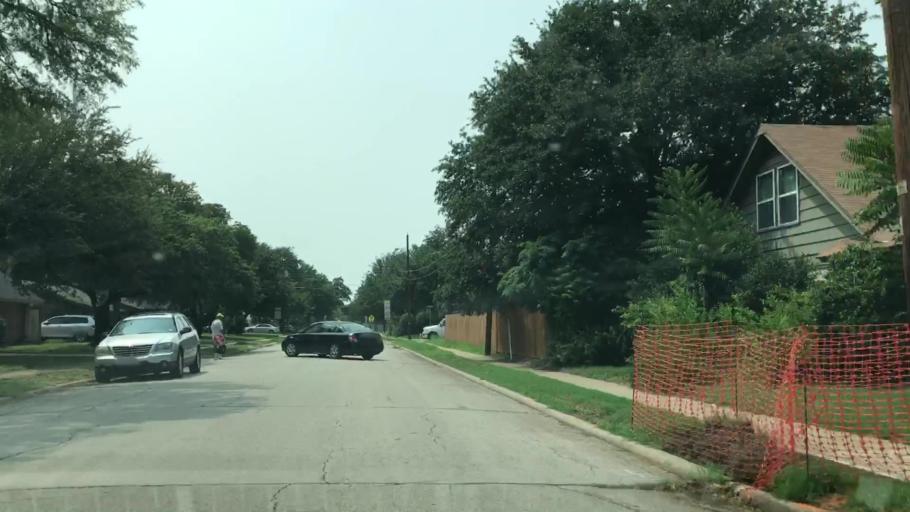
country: US
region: Texas
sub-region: Dallas County
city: Irving
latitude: 32.8520
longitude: -96.9634
